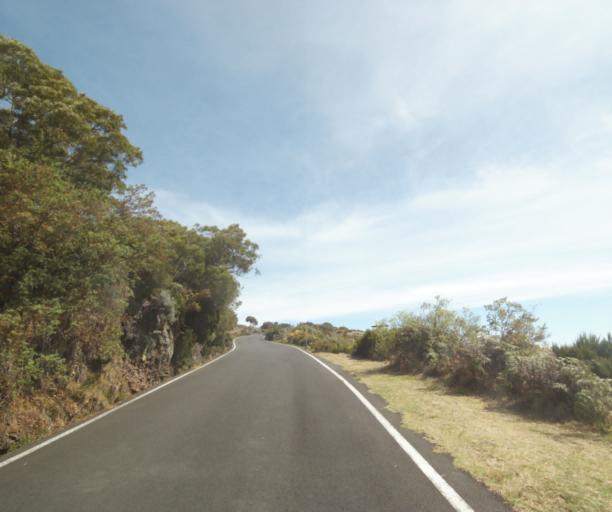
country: RE
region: Reunion
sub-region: Reunion
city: Trois-Bassins
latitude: -21.0676
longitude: 55.3787
